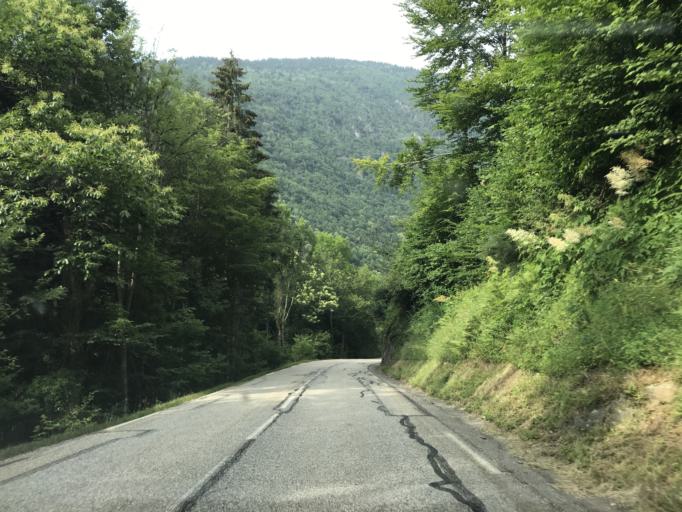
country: FR
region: Rhone-Alpes
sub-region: Departement de l'Isere
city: Allevard
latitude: 45.3807
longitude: 6.0926
